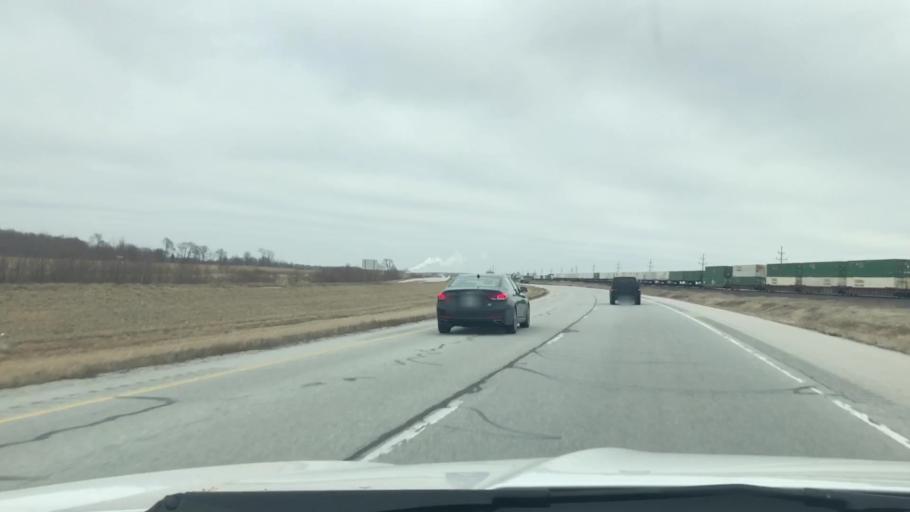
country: US
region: Indiana
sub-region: Cass County
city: Georgetown
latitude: 40.6830
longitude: -86.4965
